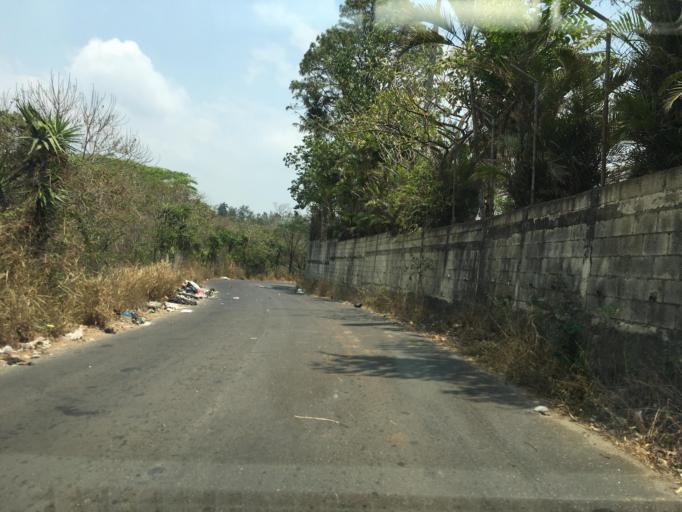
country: GT
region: Santa Rosa
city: Pueblo Nuevo Vinas
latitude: 14.3177
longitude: -90.5353
